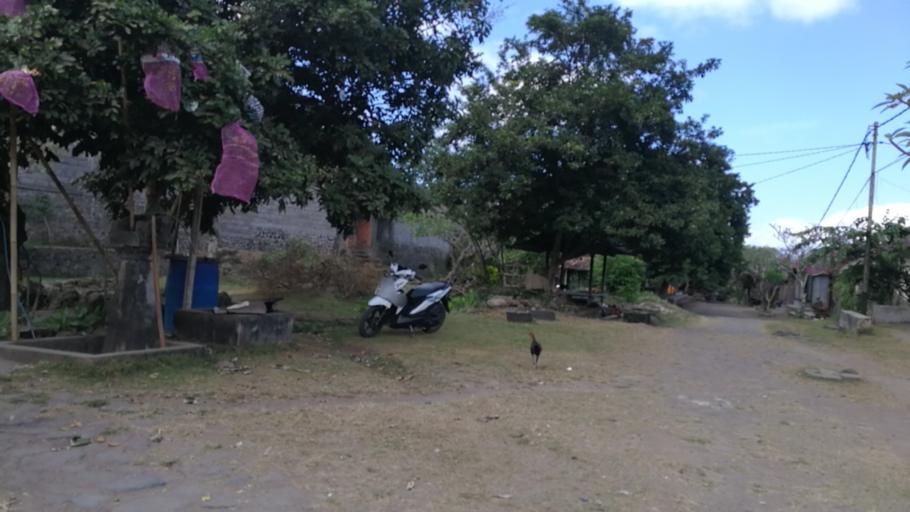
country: ID
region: Bali
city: Banjar Pegeringsingan
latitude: -8.4741
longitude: 115.5670
